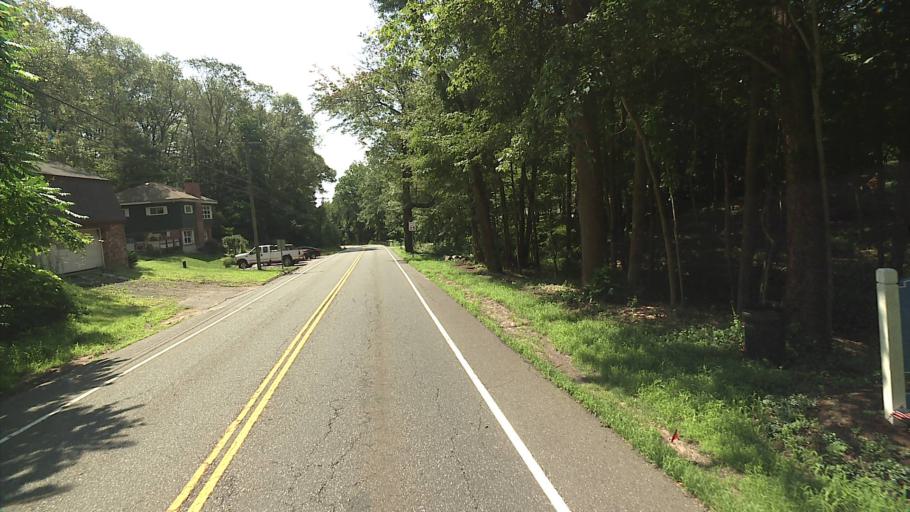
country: US
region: Connecticut
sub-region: Middlesex County
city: Deep River Center
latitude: 41.3528
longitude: -72.4450
